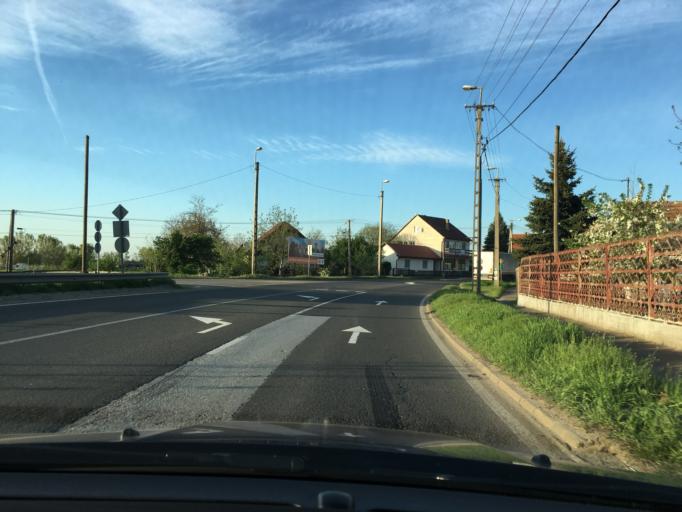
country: HU
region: Hajdu-Bihar
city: Mikepercs
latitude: 47.4362
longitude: 21.6285
